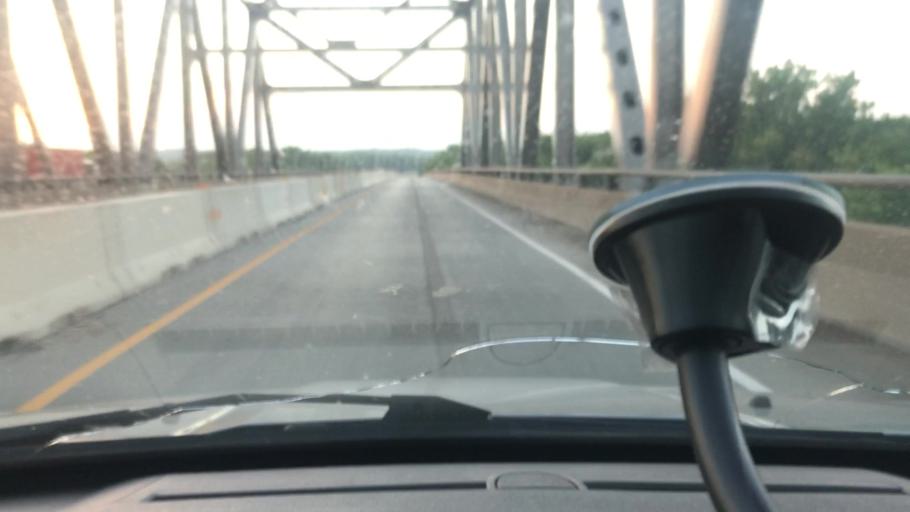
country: US
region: Illinois
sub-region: Tazewell County
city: North Pekin
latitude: 40.6359
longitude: -89.6232
